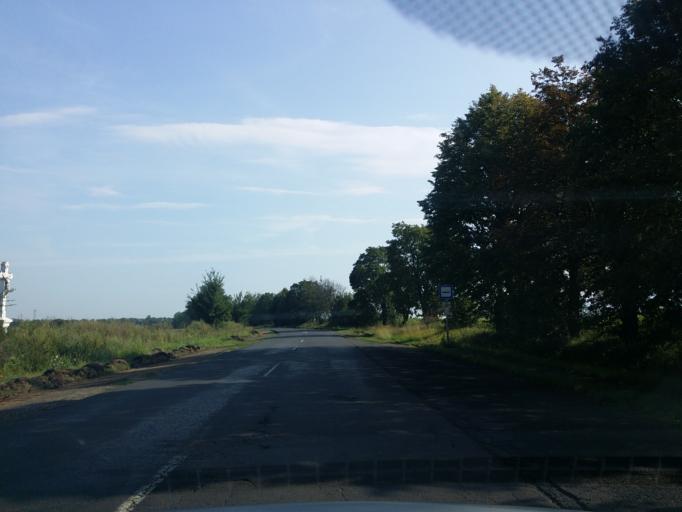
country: HU
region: Borsod-Abauj-Zemplen
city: Abaujszanto
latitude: 48.3554
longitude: 21.2147
